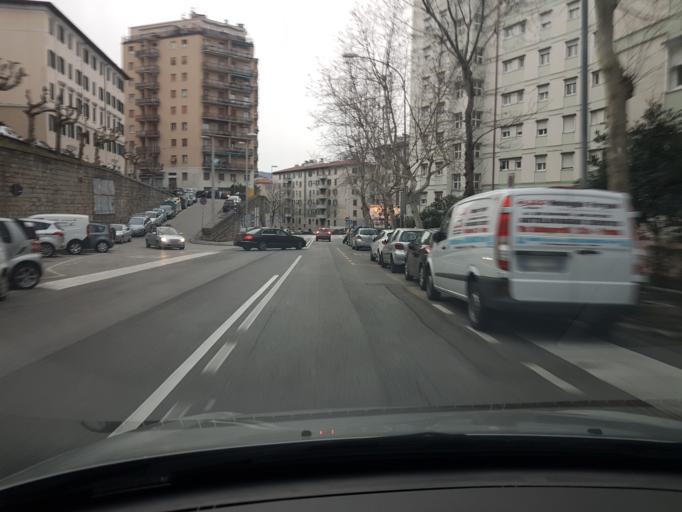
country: IT
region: Friuli Venezia Giulia
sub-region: Provincia di Trieste
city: Trieste
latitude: 45.6391
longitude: 13.7685
